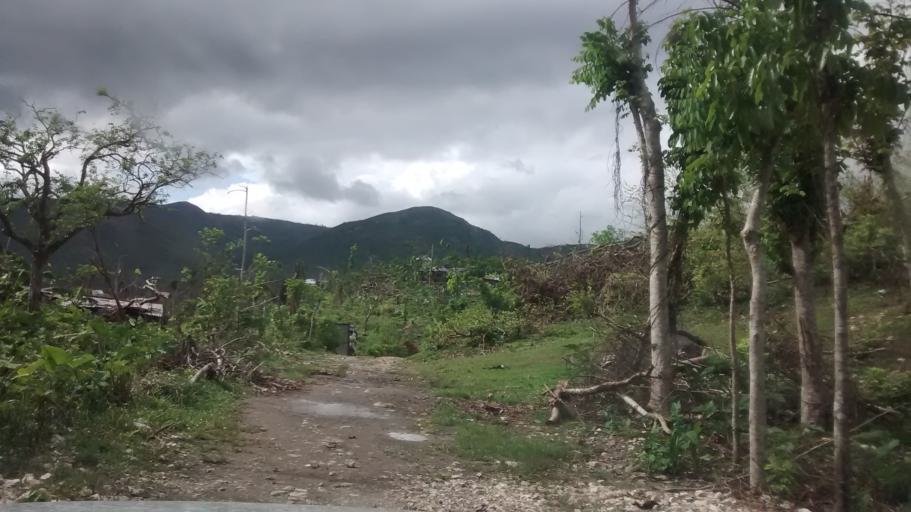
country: HT
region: Grandans
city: Moron
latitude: 18.5589
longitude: -74.2703
